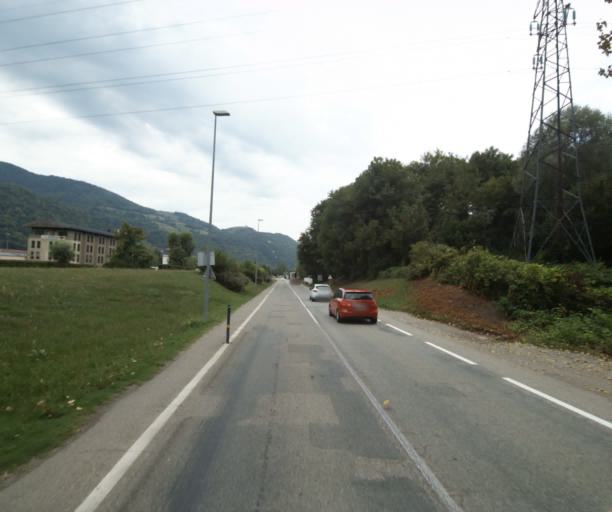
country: FR
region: Rhone-Alpes
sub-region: Departement de l'Isere
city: Domene
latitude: 45.2038
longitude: 5.8253
